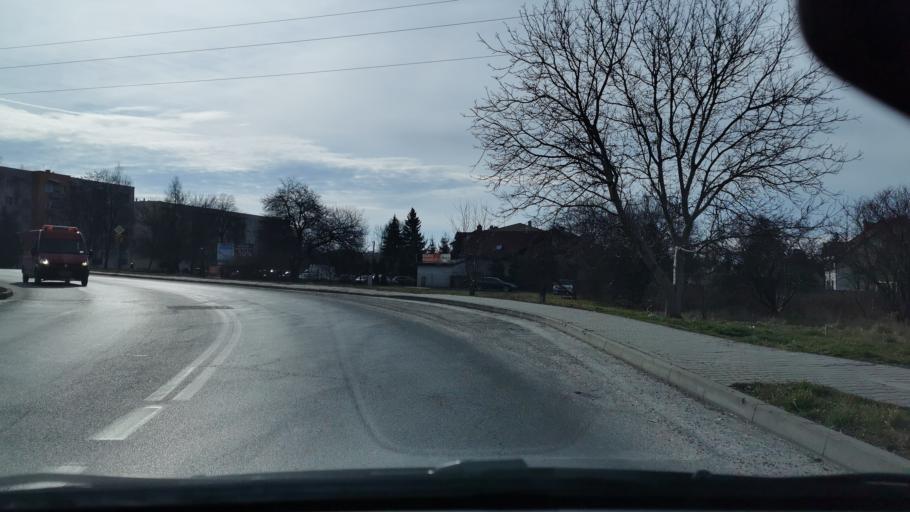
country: PL
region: Lublin Voivodeship
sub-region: Powiat lubelski
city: Lublin
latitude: 51.2054
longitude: 22.5426
